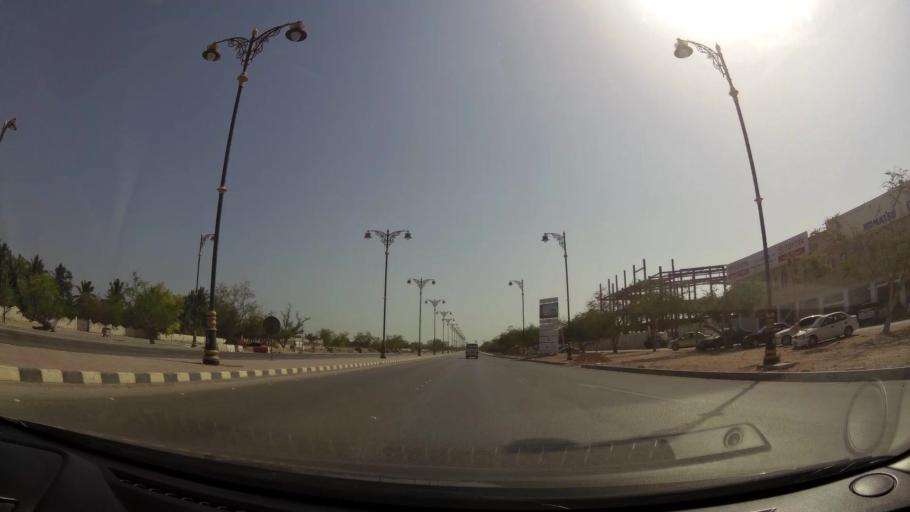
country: OM
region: Zufar
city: Salalah
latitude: 17.0139
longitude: 54.0519
